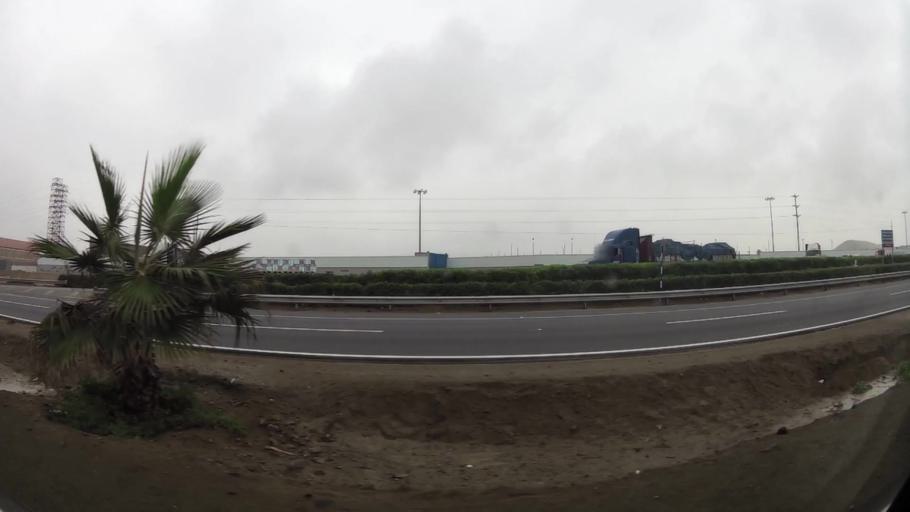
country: PE
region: Lima
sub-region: Lima
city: Punta Hermosa
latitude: -12.3146
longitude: -76.8325
